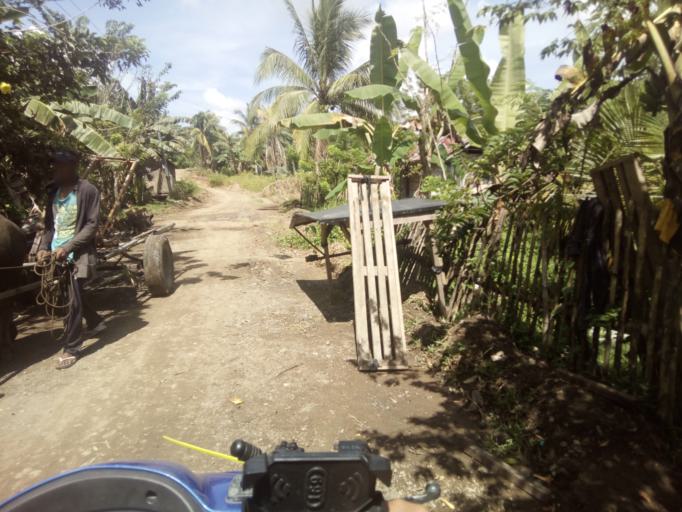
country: PH
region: Caraga
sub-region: Province of Agusan del Sur
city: Santa Josefa
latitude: 7.9798
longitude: 125.9751
